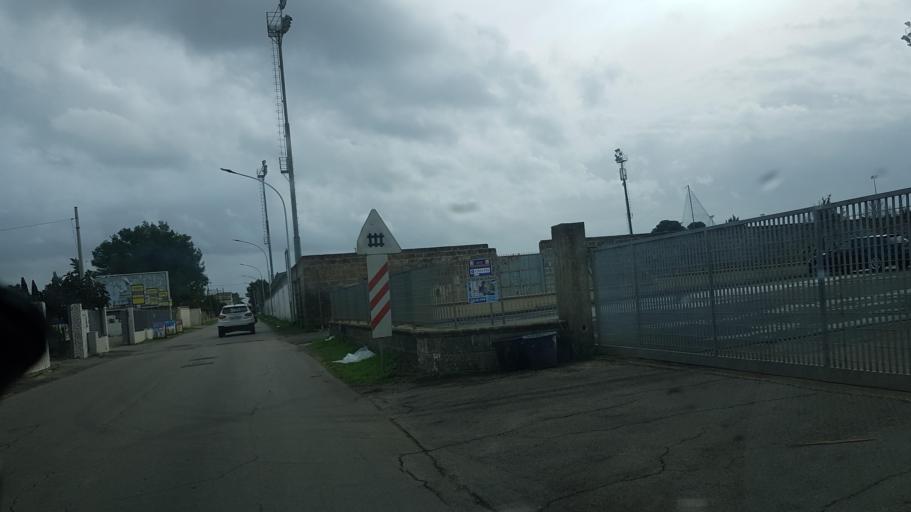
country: IT
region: Apulia
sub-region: Provincia di Lecce
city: Carmiano
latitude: 40.3446
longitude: 18.0521
